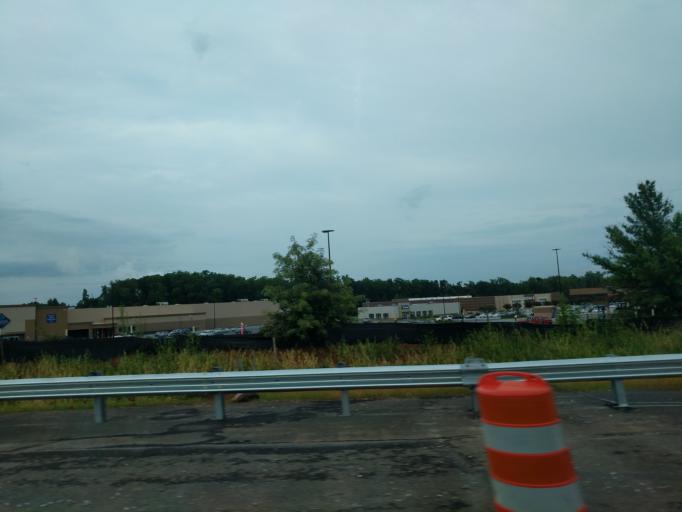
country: US
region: South Carolina
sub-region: Greenville County
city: Mauldin
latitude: 34.8239
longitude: -82.2905
